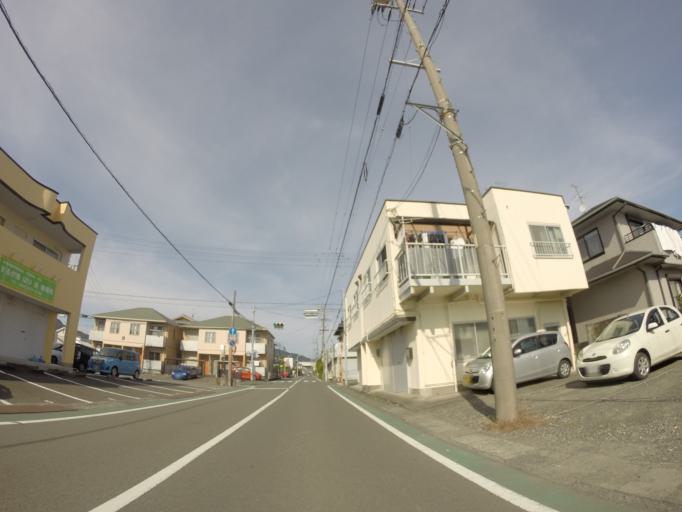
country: JP
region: Shizuoka
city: Shizuoka-shi
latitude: 34.9340
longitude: 138.3774
